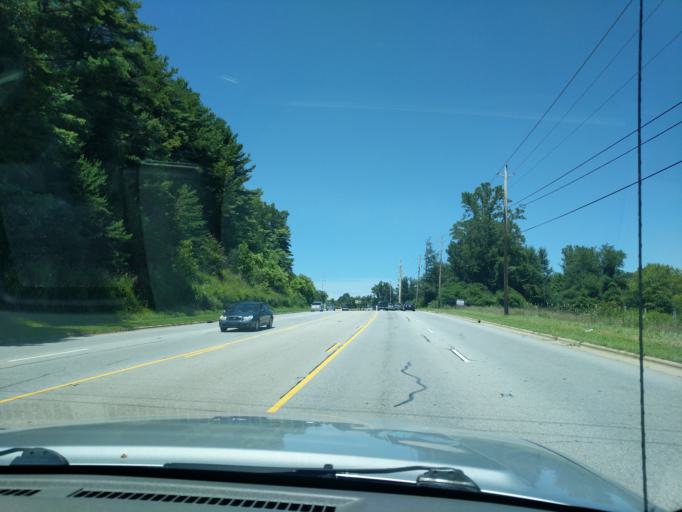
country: US
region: North Carolina
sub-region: Buncombe County
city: Royal Pines
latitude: 35.4555
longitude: -82.5108
